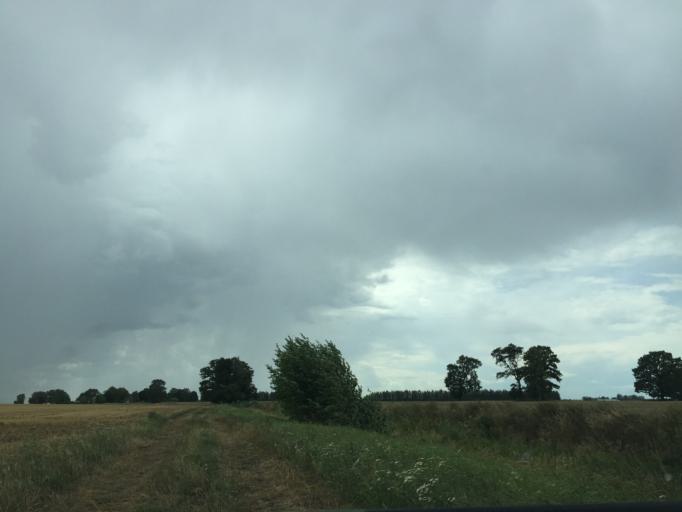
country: LT
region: Siauliu apskritis
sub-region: Joniskis
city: Joniskis
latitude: 56.2932
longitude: 23.7275
